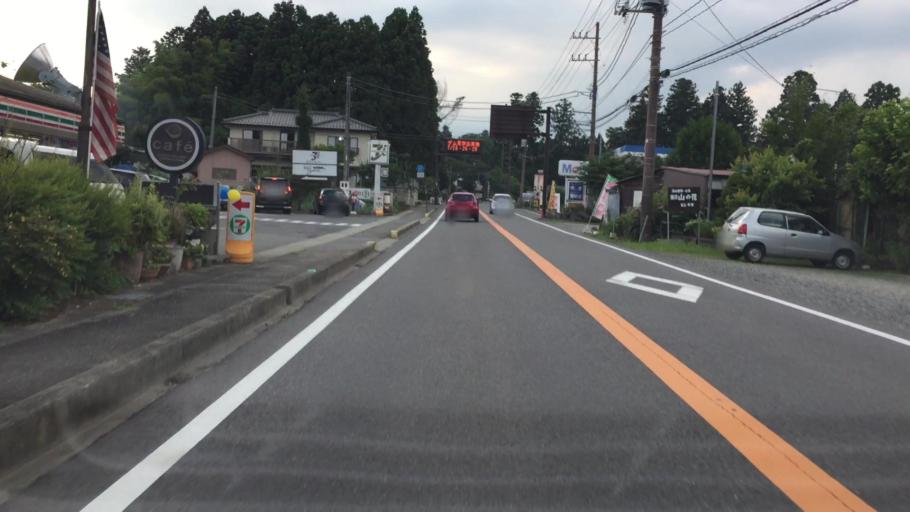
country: JP
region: Tochigi
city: Kuroiso
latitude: 37.0078
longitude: 140.0321
